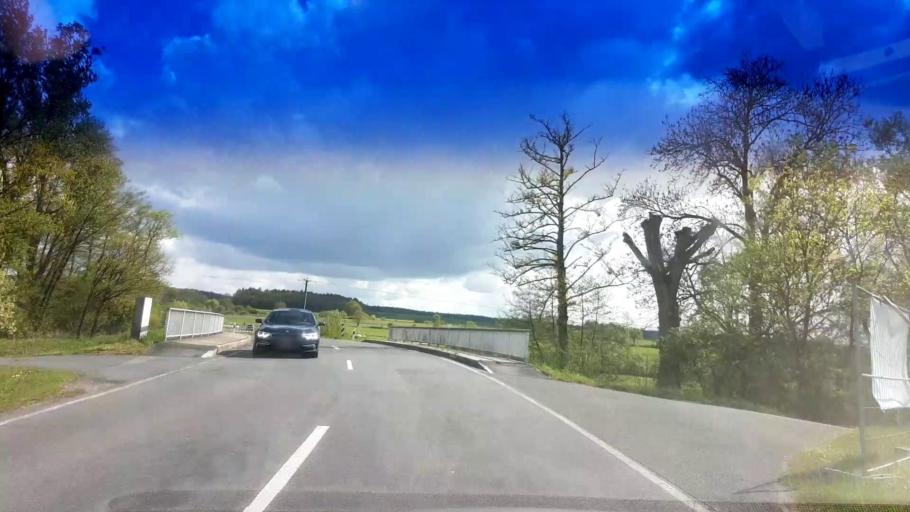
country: DE
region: Bavaria
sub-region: Upper Franconia
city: Frensdorf
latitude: 49.8230
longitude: 10.8414
